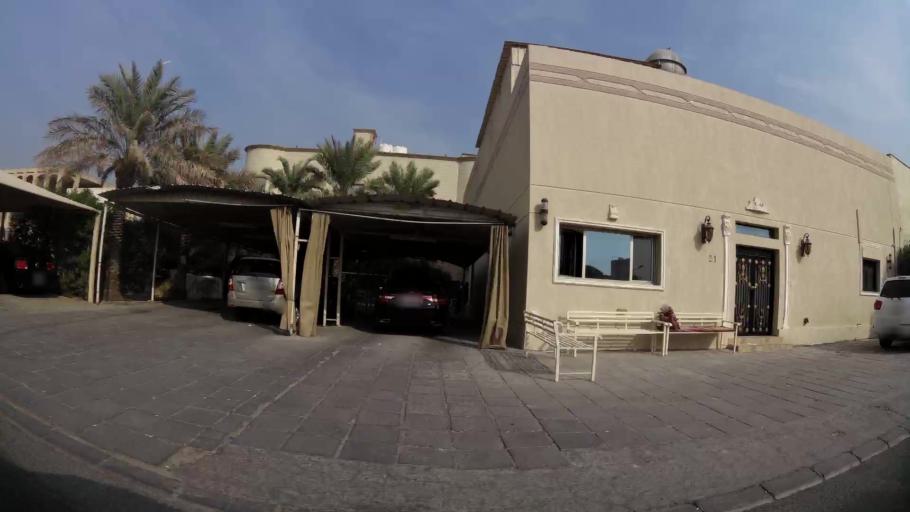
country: KW
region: Al Farwaniyah
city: Al Farwaniyah
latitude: 29.2915
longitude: 47.9545
